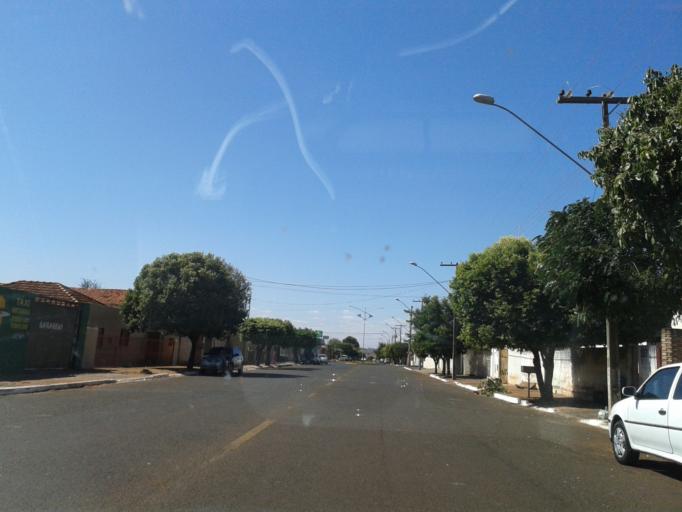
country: BR
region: Minas Gerais
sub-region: Santa Vitoria
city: Santa Vitoria
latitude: -18.8451
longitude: -50.1253
